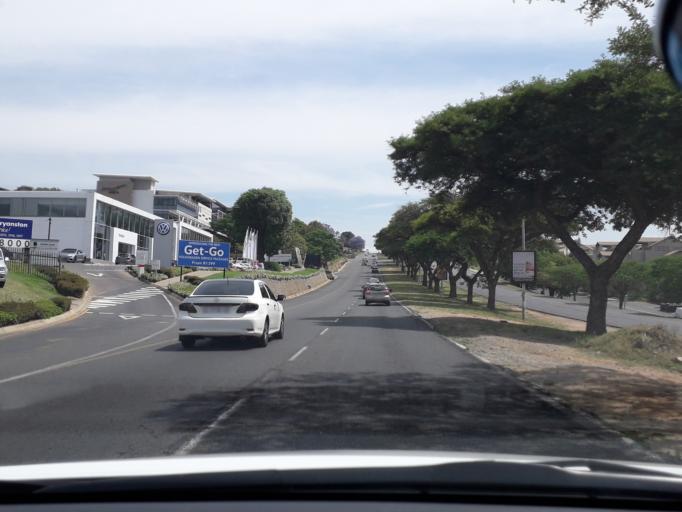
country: ZA
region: Gauteng
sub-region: City of Johannesburg Metropolitan Municipality
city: Midrand
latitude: -26.0702
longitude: 28.0261
